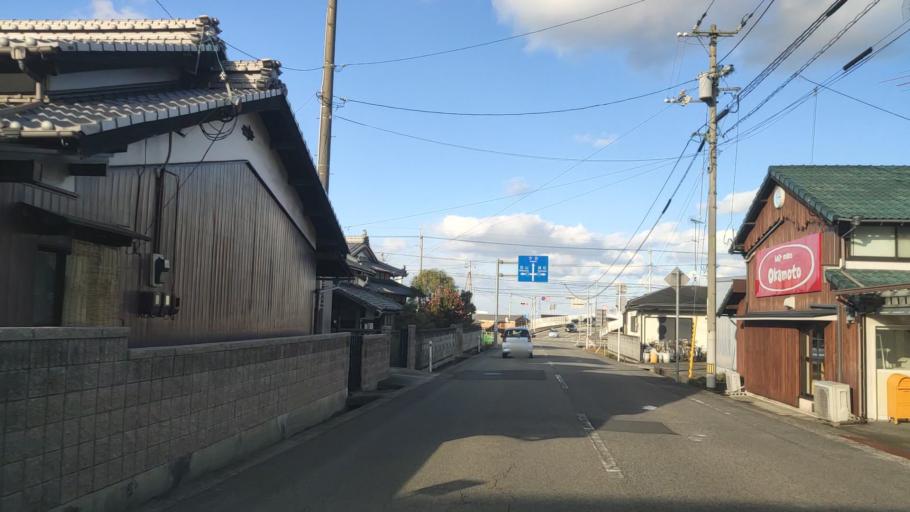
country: JP
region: Ehime
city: Saijo
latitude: 33.8946
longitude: 133.1323
